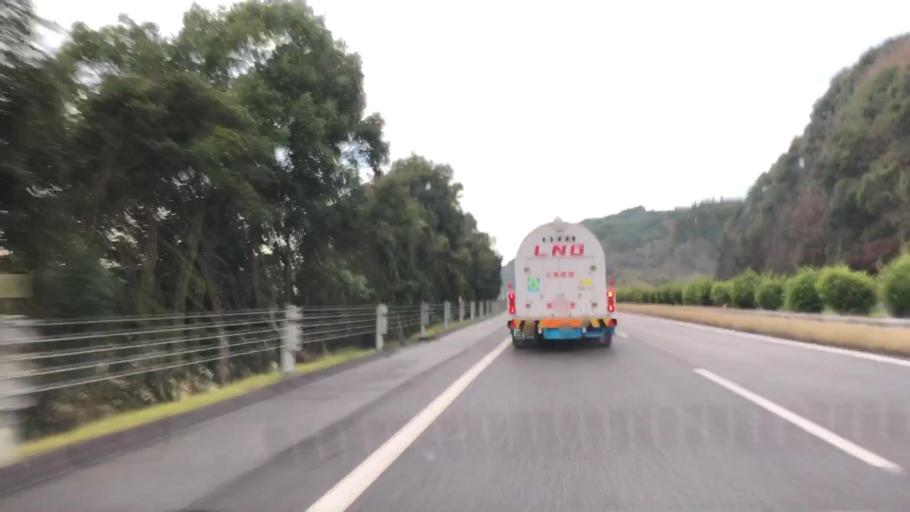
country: JP
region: Saga Prefecture
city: Takeocho-takeo
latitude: 33.2658
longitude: 130.0873
